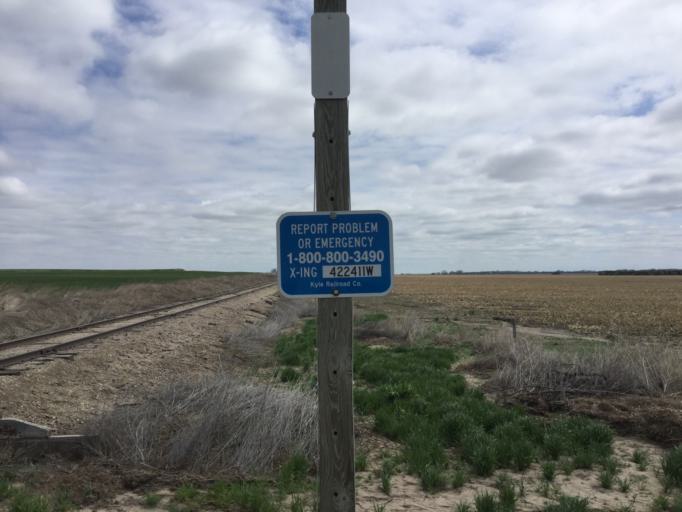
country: US
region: Kansas
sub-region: Osborne County
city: Osborne
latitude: 39.4422
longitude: -98.6758
